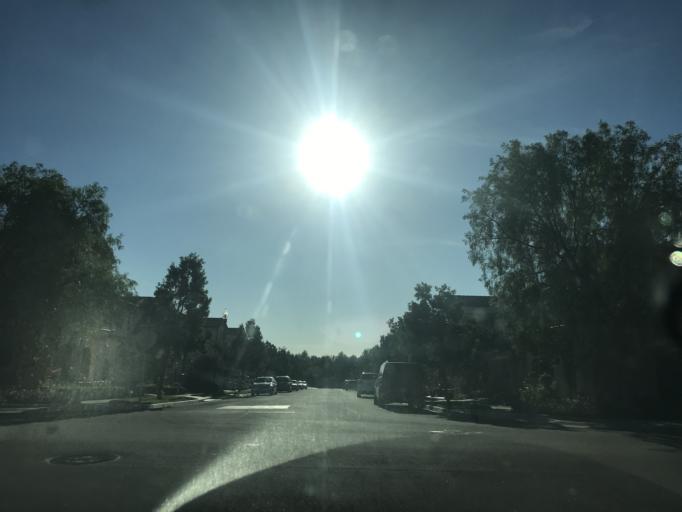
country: US
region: California
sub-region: Orange County
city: North Tustin
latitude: 33.7100
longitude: -117.7390
